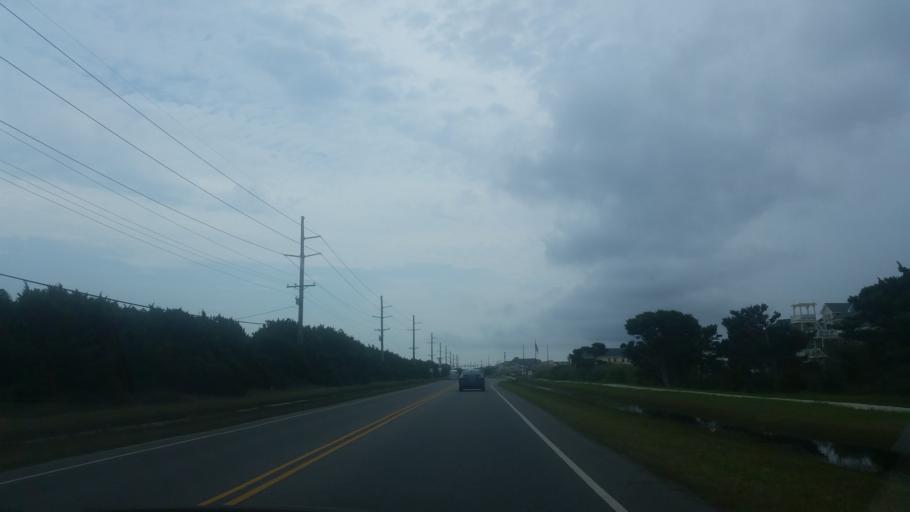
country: US
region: North Carolina
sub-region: Dare County
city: Buxton
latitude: 35.3377
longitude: -75.5058
